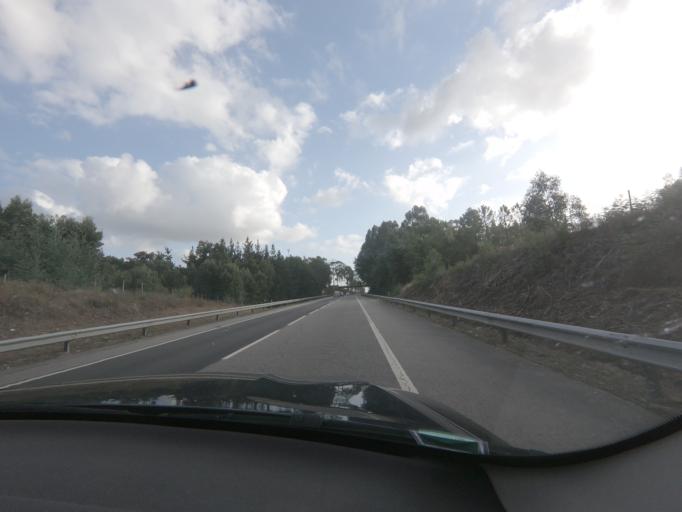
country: PT
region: Viseu
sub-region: Concelho de Tondela
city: Tondela
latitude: 40.5714
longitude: -8.0351
